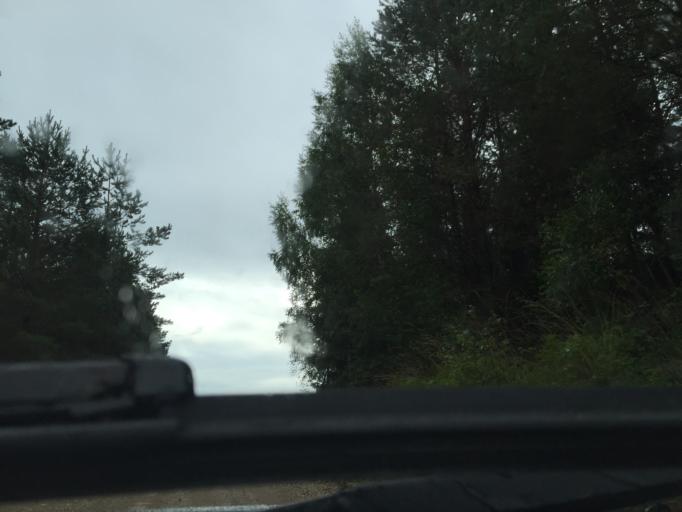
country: LV
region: Preilu Rajons
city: Jaunaglona
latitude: 56.2579
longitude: 27.1568
